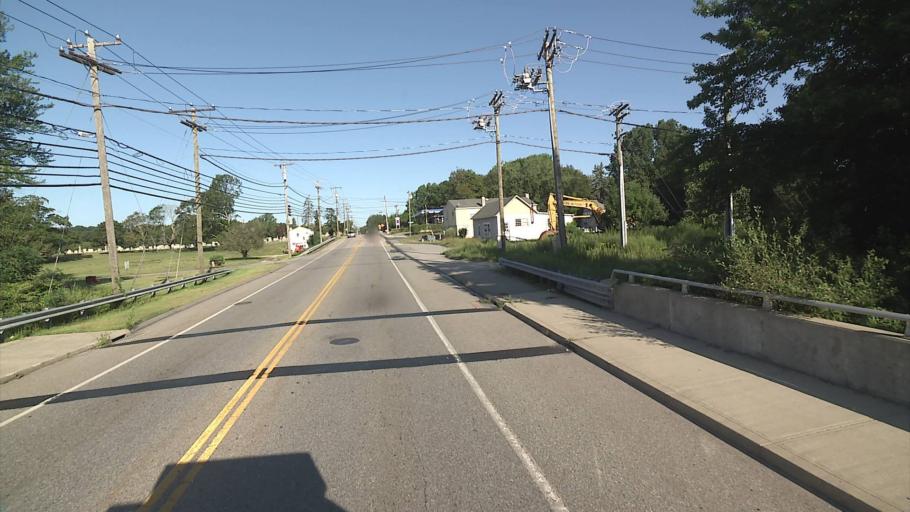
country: US
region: Connecticut
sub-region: New London County
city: Central Waterford
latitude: 41.3460
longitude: -72.1387
